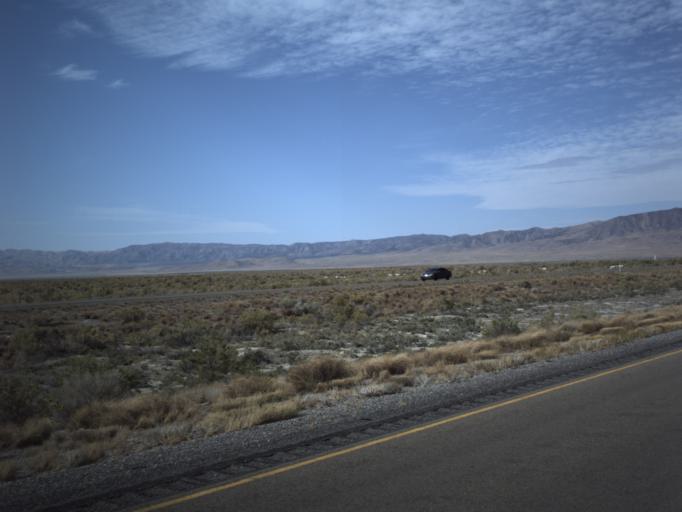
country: US
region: Utah
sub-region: Tooele County
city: Grantsville
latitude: 40.7544
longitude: -112.7356
